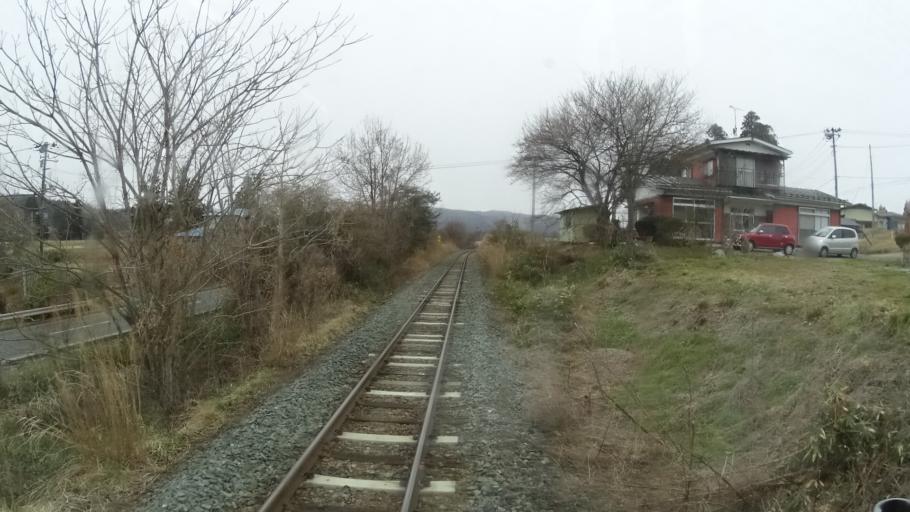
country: JP
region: Iwate
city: Hanamaki
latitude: 39.3778
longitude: 141.2444
